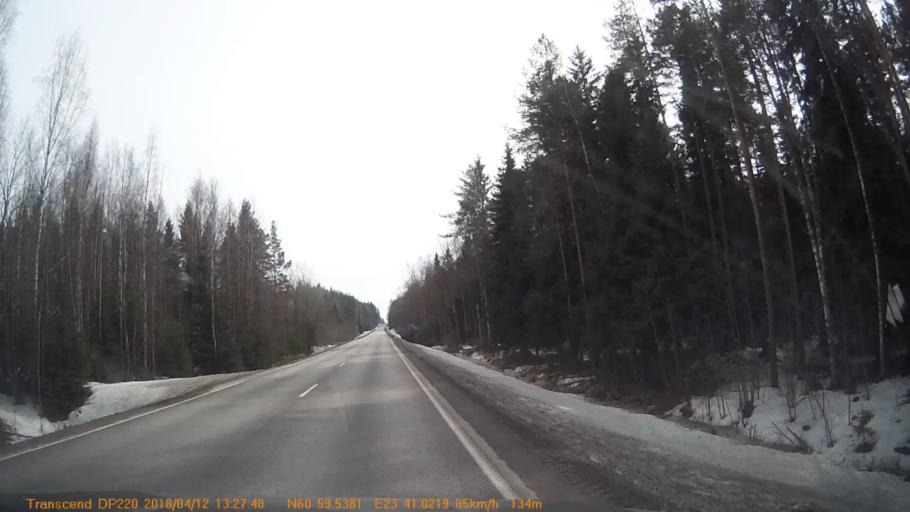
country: FI
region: Pirkanmaa
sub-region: Etelae-Pirkanmaa
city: Kylmaekoski
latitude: 60.9921
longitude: 23.6839
